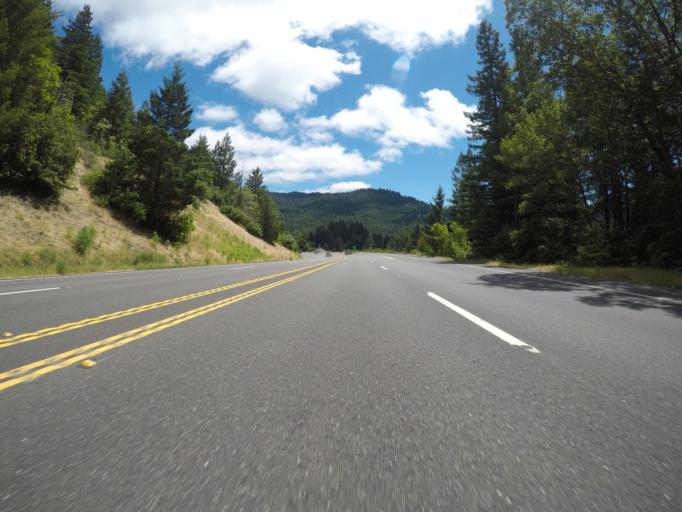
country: US
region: California
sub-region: Humboldt County
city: Redway
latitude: 40.2694
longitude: -123.8743
